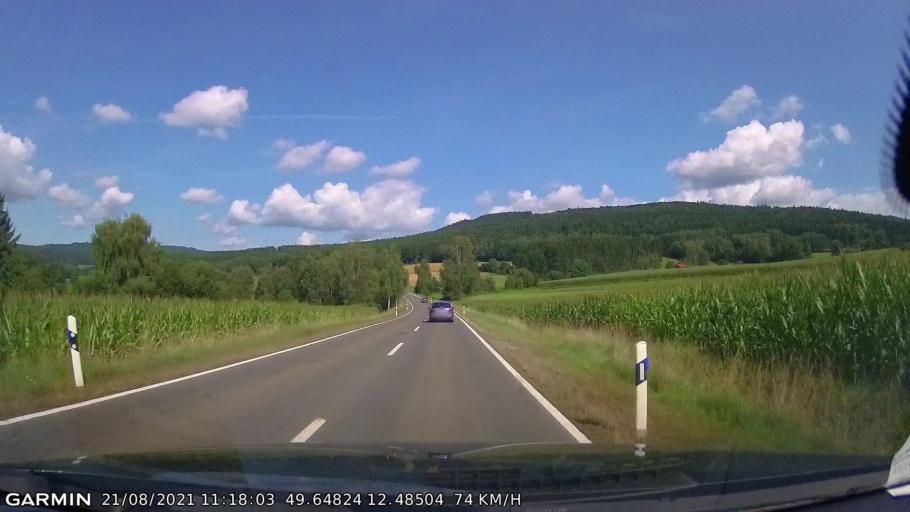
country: DE
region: Bavaria
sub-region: Upper Palatinate
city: Waidhaus
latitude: 49.6485
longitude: 12.4850
